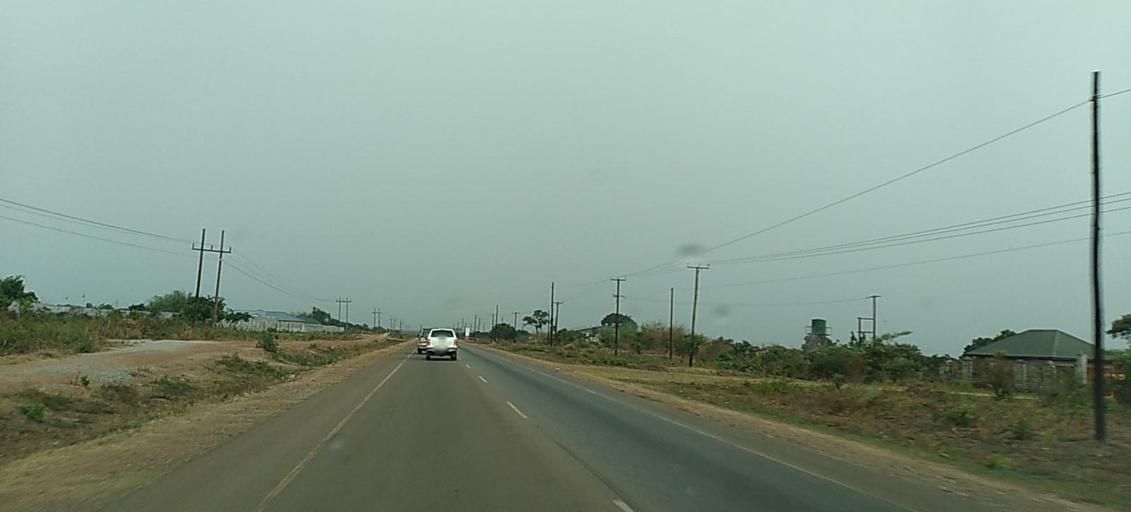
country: ZM
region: Copperbelt
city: Kalulushi
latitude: -12.8350
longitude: 28.1226
